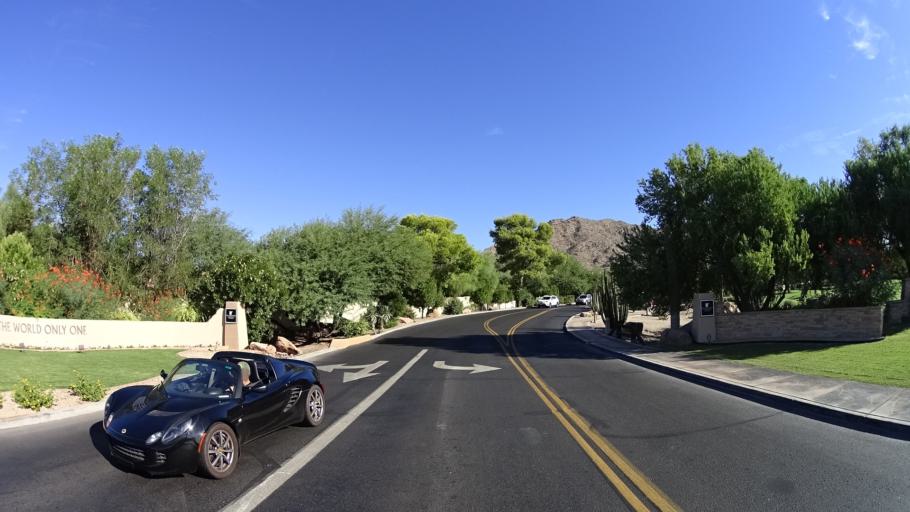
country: US
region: Arizona
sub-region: Maricopa County
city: Paradise Valley
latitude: 33.5313
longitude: -111.9666
